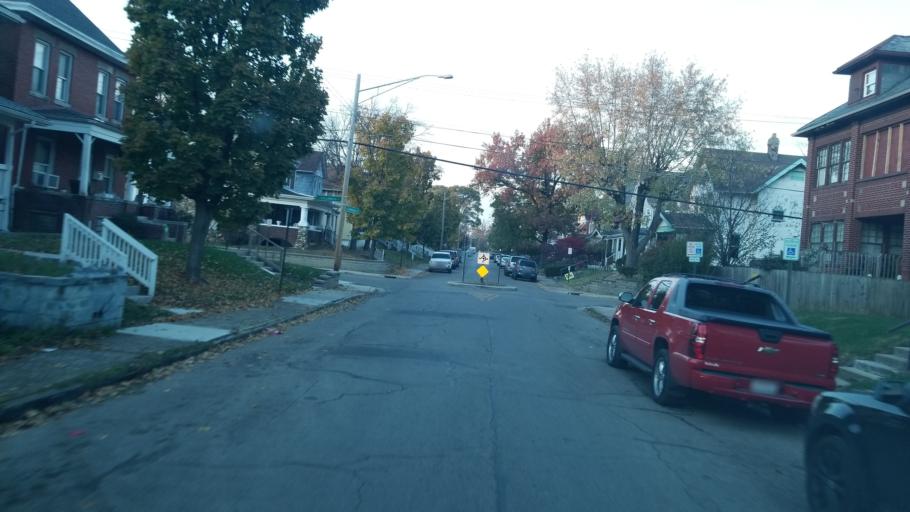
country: US
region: Ohio
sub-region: Franklin County
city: Columbus
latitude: 39.9454
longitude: -82.9661
